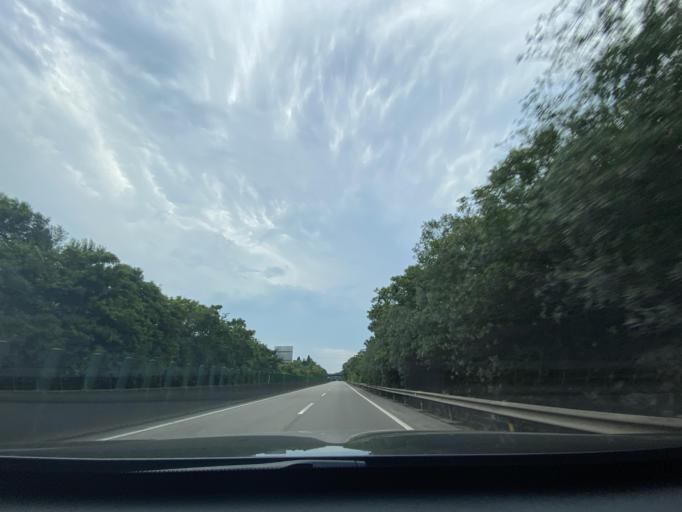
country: CN
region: Sichuan
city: Neijiang
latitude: 29.6608
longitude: 104.9814
